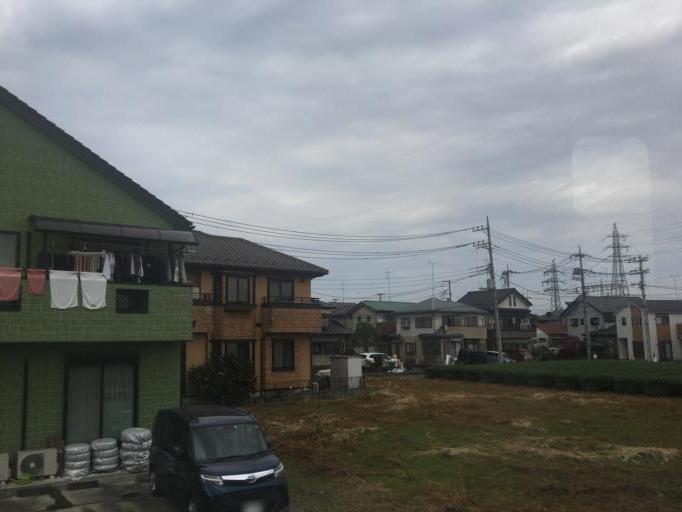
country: JP
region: Saitama
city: Hanno
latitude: 35.8468
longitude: 139.3286
